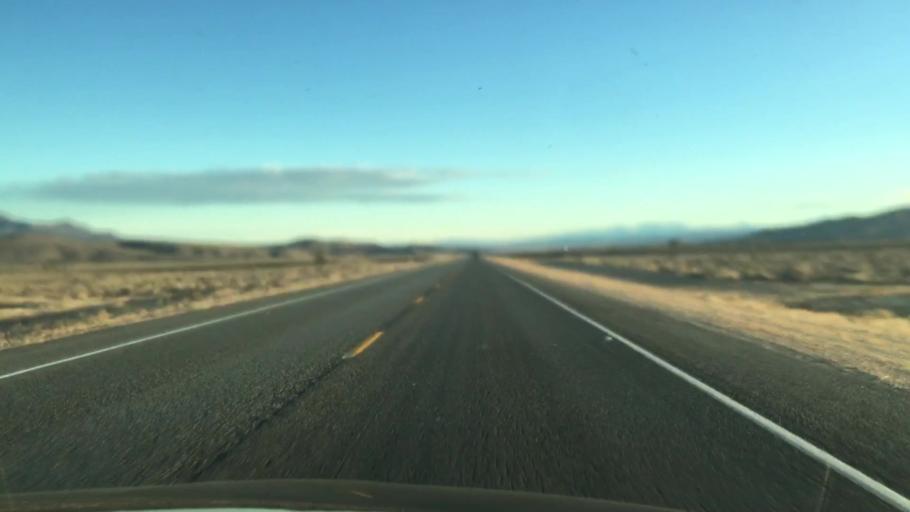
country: US
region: Nevada
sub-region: Esmeralda County
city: Goldfield
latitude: 37.5939
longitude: -117.2099
